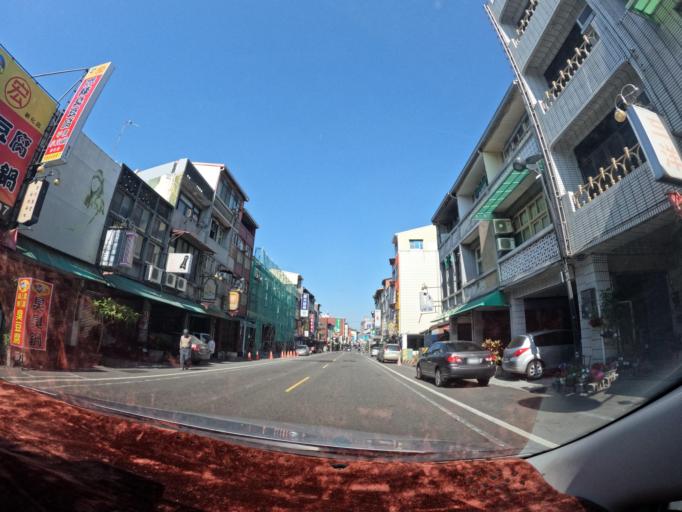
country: TW
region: Taiwan
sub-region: Tainan
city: Tainan
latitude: 23.0368
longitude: 120.3079
